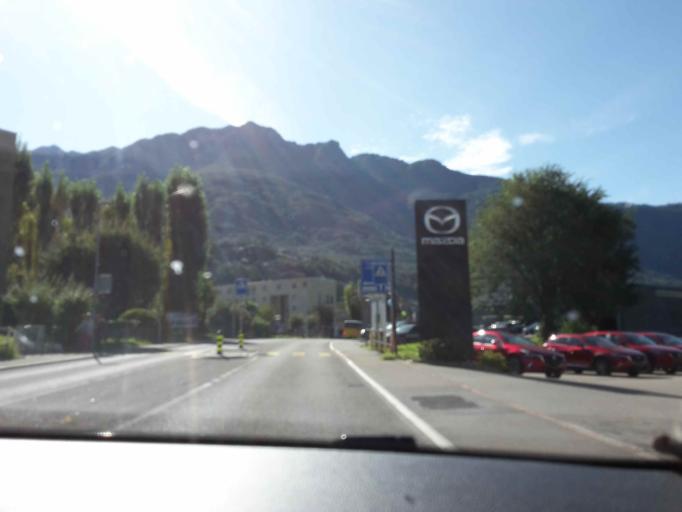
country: CH
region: Ticino
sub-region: Bellinzona District
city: Giubiasco
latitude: 46.1801
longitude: 9.0139
